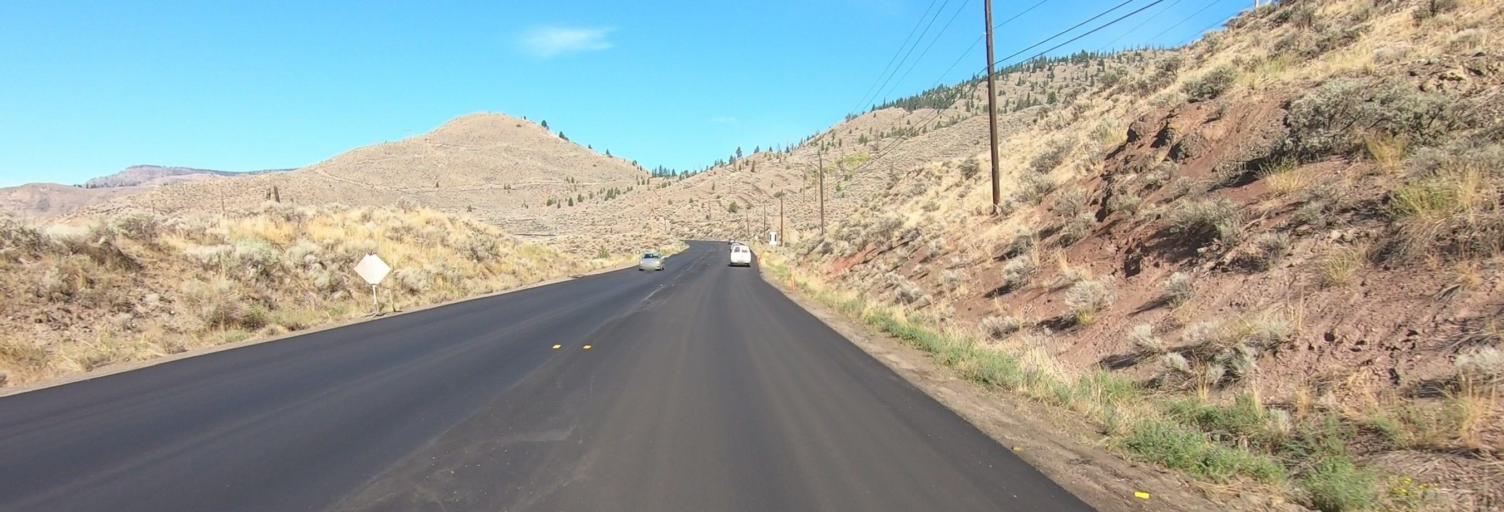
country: CA
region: British Columbia
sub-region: Thompson-Nicola Regional District
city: Ashcroft
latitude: 50.7965
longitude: -121.0993
